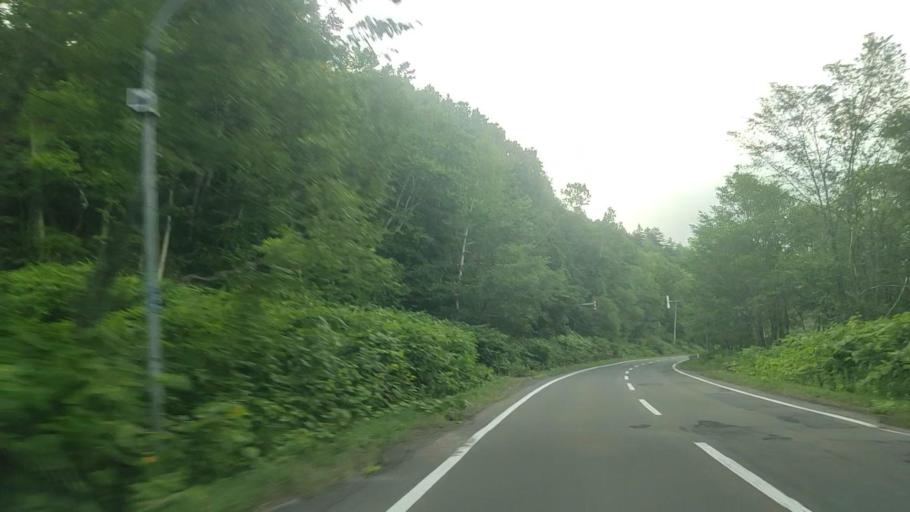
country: JP
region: Hokkaido
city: Bibai
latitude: 43.1163
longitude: 142.0986
